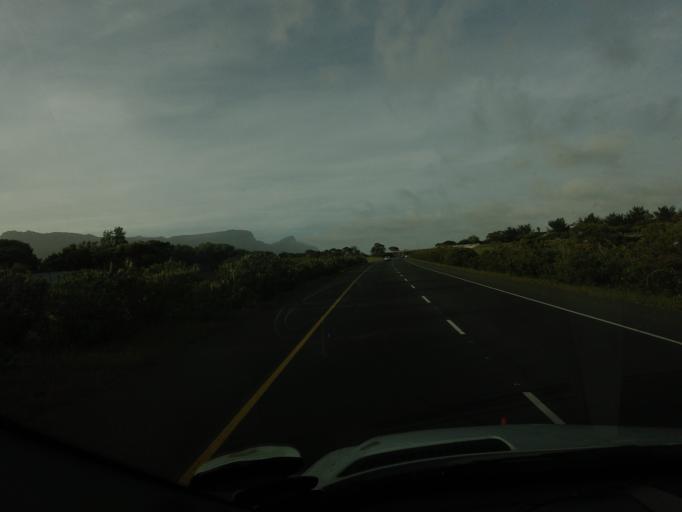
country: ZA
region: Western Cape
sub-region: City of Cape Town
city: Bergvliet
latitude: -34.0338
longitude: 18.4441
